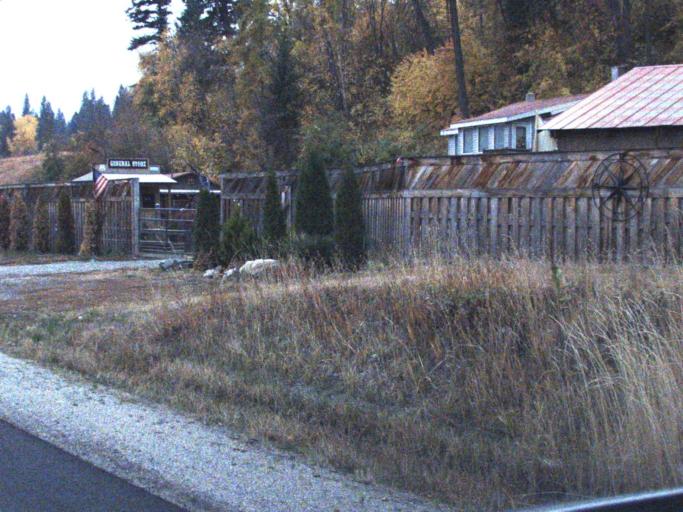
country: US
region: Washington
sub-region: Stevens County
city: Kettle Falls
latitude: 48.6693
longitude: -118.1161
